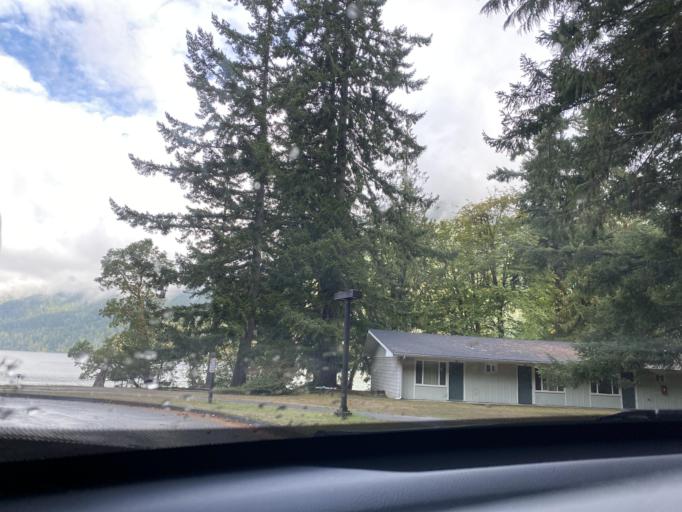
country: CA
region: British Columbia
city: Sooke
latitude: 48.0582
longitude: -123.7985
